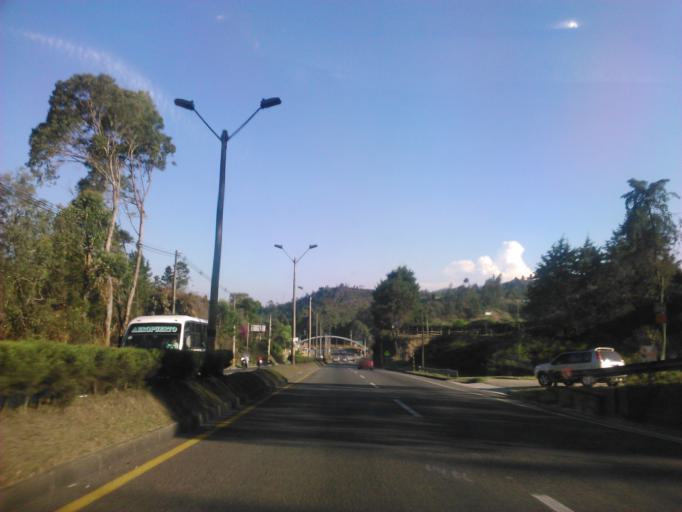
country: CO
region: Antioquia
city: Guarne
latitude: 6.3093
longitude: -75.4602
